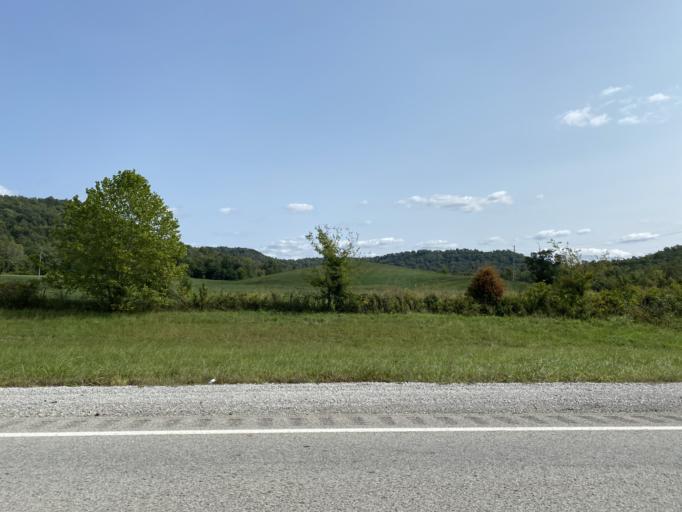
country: US
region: Kentucky
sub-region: Marion County
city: Lebanon
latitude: 37.4942
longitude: -85.2957
